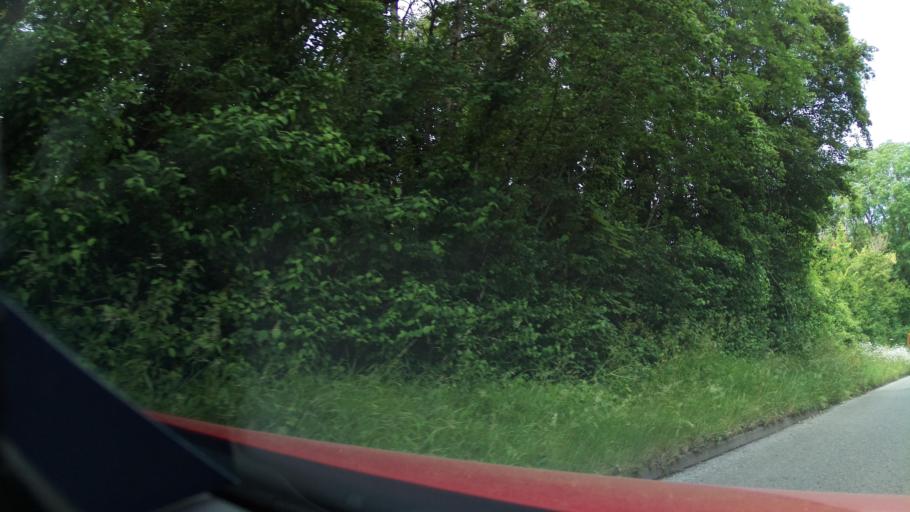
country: GB
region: Wales
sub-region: Vale of Glamorgan
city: Rhoose
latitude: 51.3931
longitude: -3.3890
